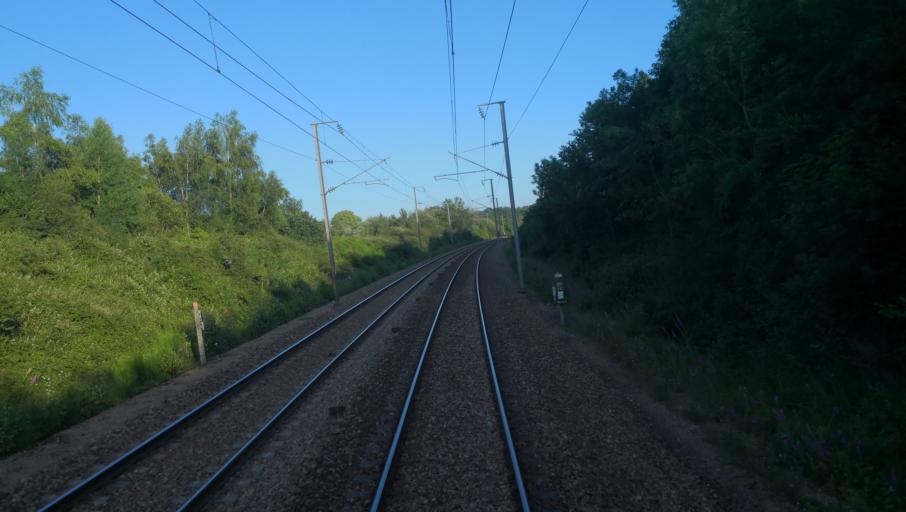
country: FR
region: Lower Normandy
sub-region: Departement du Calvados
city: Moyaux
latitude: 49.1165
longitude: 0.3419
